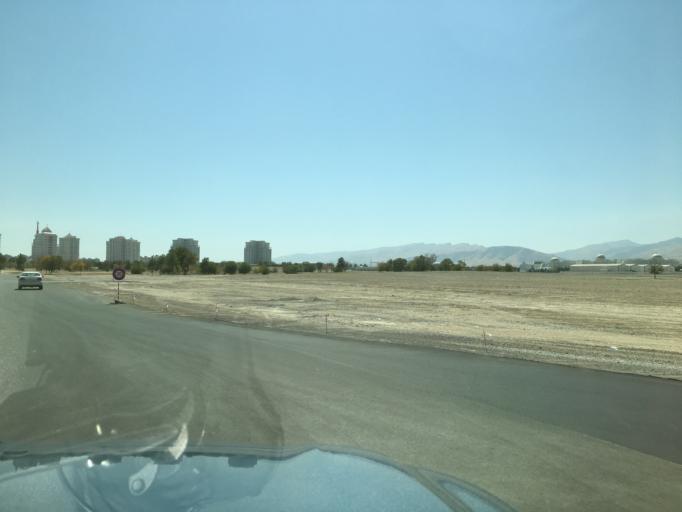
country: TM
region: Ahal
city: Ashgabat
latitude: 37.8908
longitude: 58.3662
